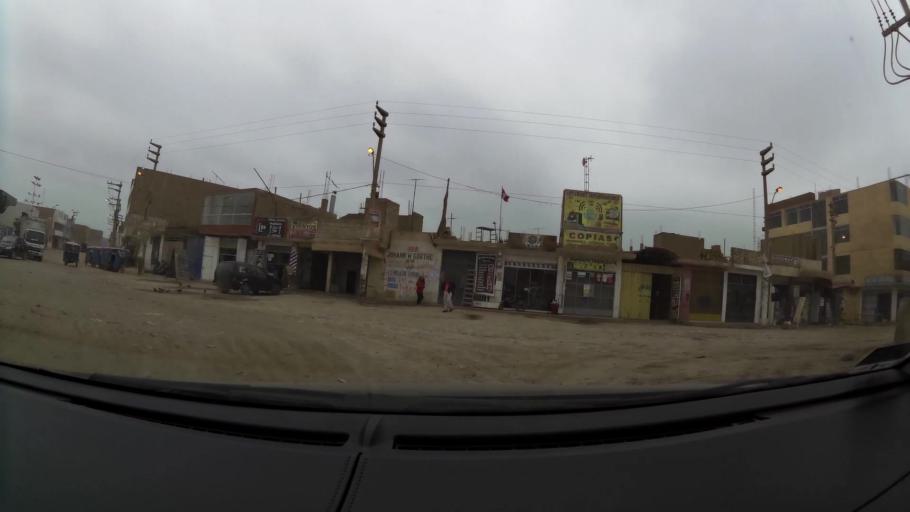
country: PE
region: Lima
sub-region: Lima
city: Independencia
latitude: -11.9684
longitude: -77.0968
